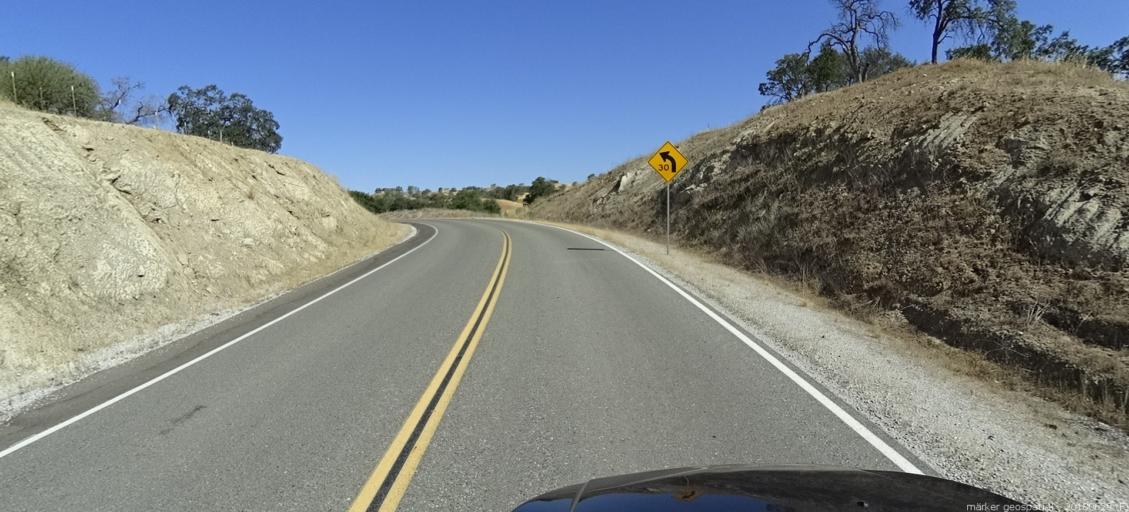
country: US
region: California
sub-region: Madera County
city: Bonadelle Ranchos-Madera Ranchos
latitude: 37.0718
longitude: -119.7920
